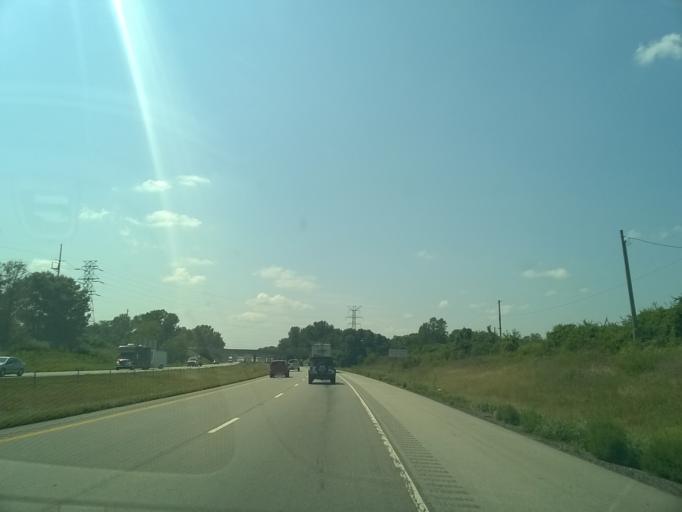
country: US
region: Indiana
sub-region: Hendricks County
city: Plainfield
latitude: 39.6624
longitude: -86.3850
